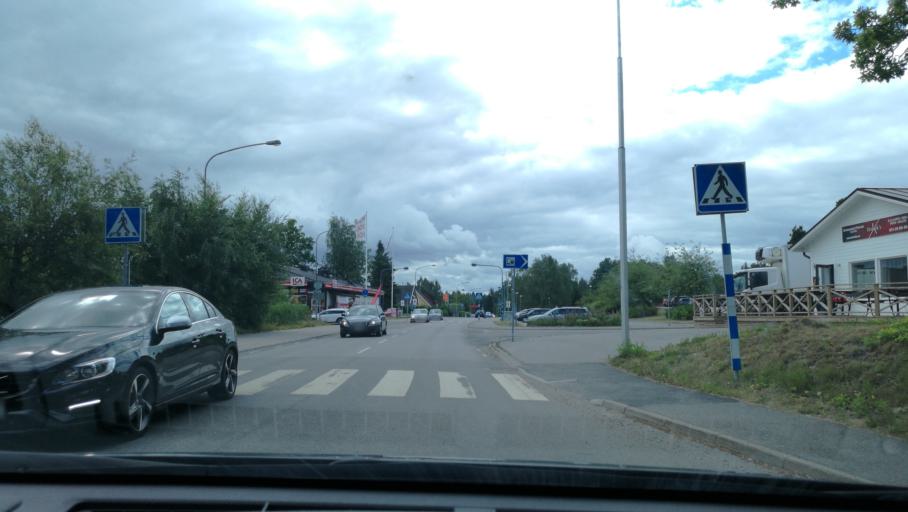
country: SE
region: OEstergoetland
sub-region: Norrkopings Kommun
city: Krokek
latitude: 58.6745
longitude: 16.3639
